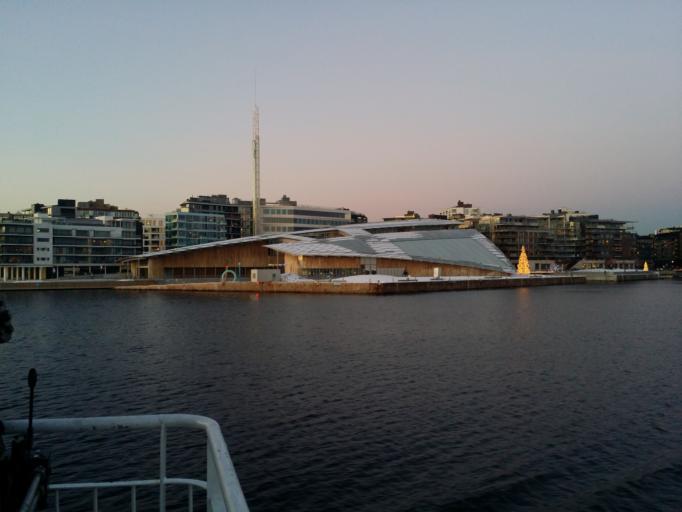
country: NO
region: Oslo
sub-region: Oslo
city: Oslo
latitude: 59.9049
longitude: 10.7225
